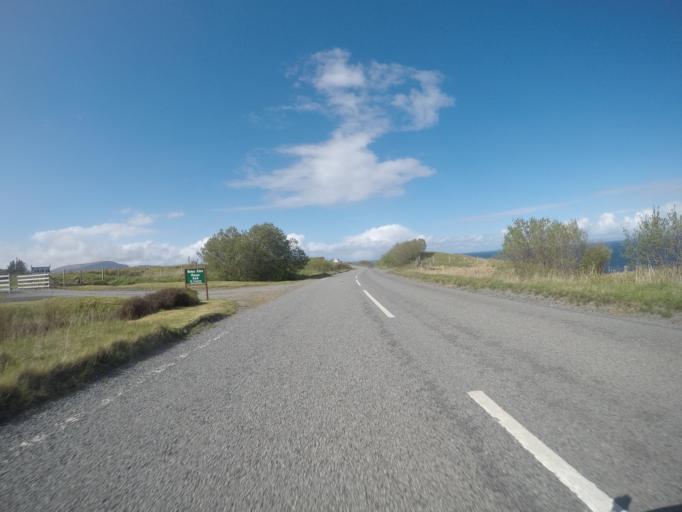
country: GB
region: Scotland
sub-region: Highland
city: Portree
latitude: 57.5923
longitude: -6.1596
